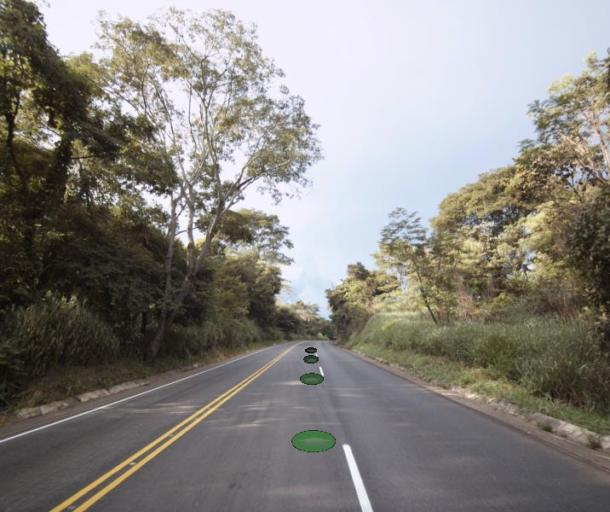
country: BR
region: Goias
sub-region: Ceres
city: Ceres
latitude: -15.1525
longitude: -49.5367
